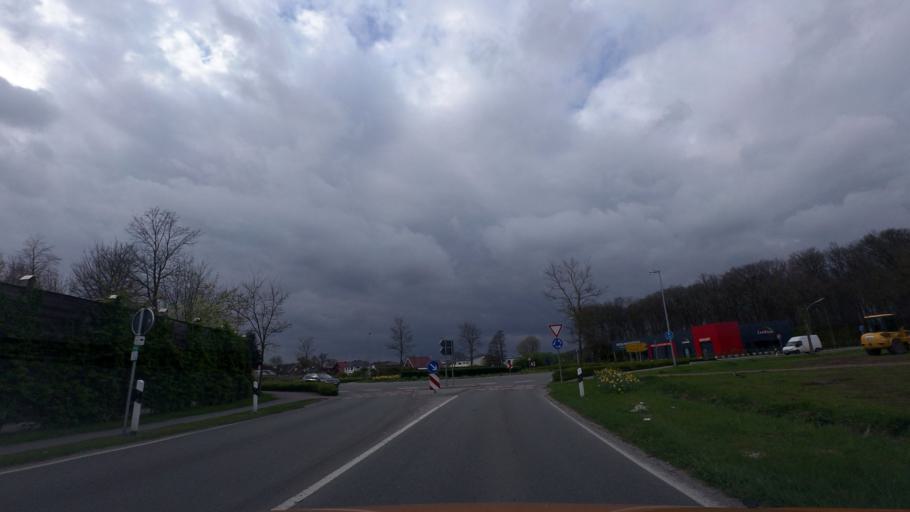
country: DE
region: Lower Saxony
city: Friesoythe
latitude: 53.0251
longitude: 7.8716
